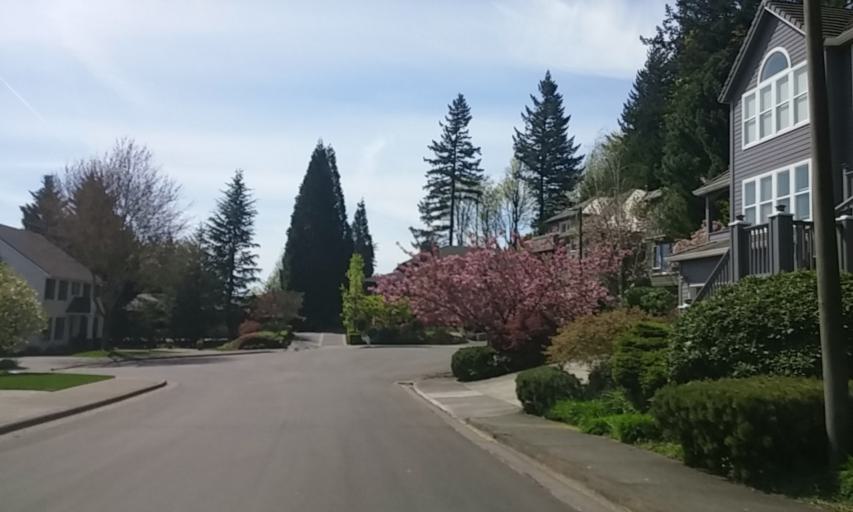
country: US
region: Oregon
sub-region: Washington County
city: West Haven-Sylvan
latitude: 45.5133
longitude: -122.7462
